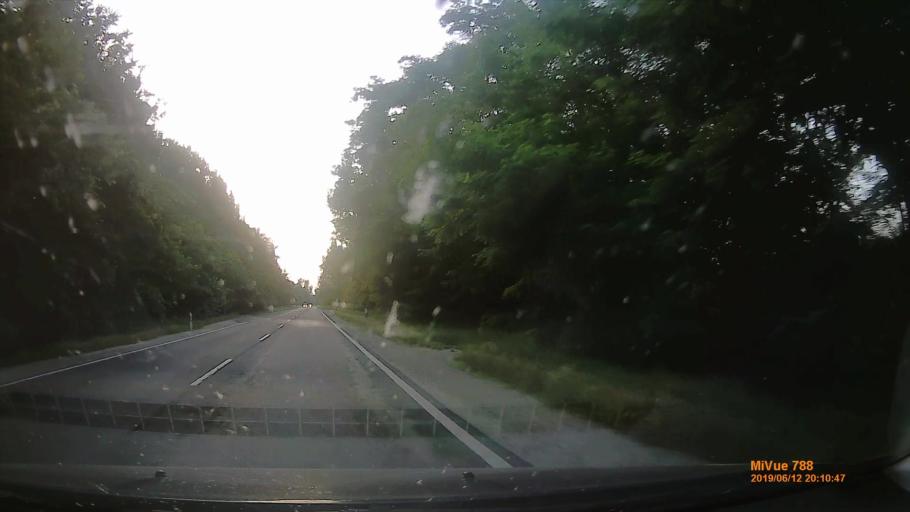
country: HU
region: Pest
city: Ocsa
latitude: 47.2687
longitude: 19.2111
